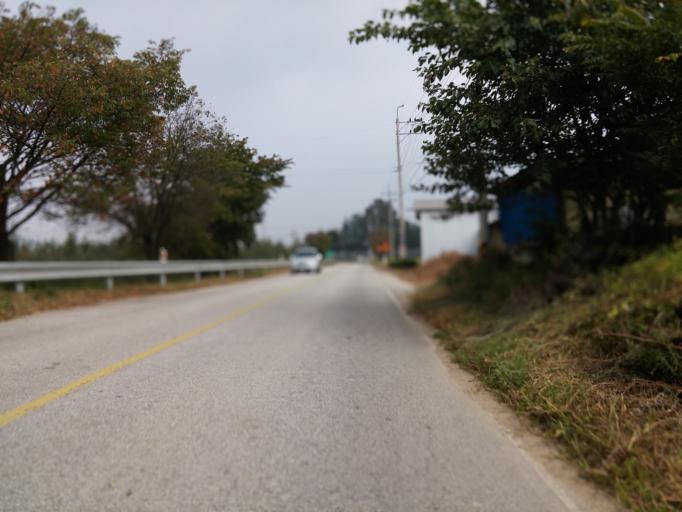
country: KR
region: Chungcheongbuk-do
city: Okcheon
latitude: 36.4065
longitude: 127.7512
